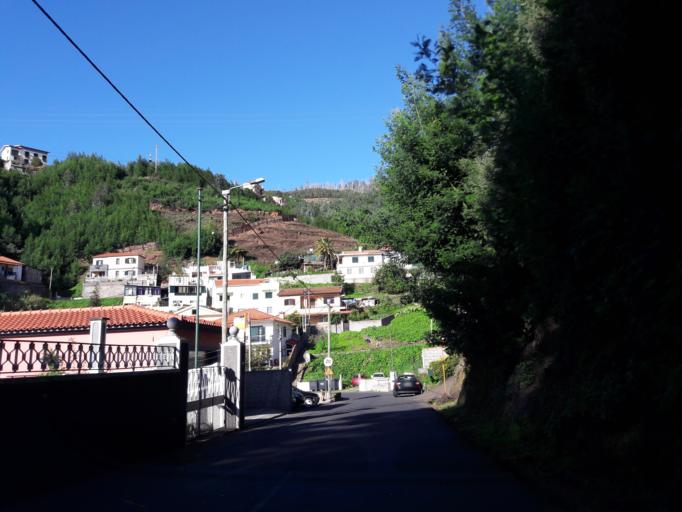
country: PT
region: Madeira
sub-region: Funchal
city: Nossa Senhora do Monte
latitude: 32.6789
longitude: -16.9081
